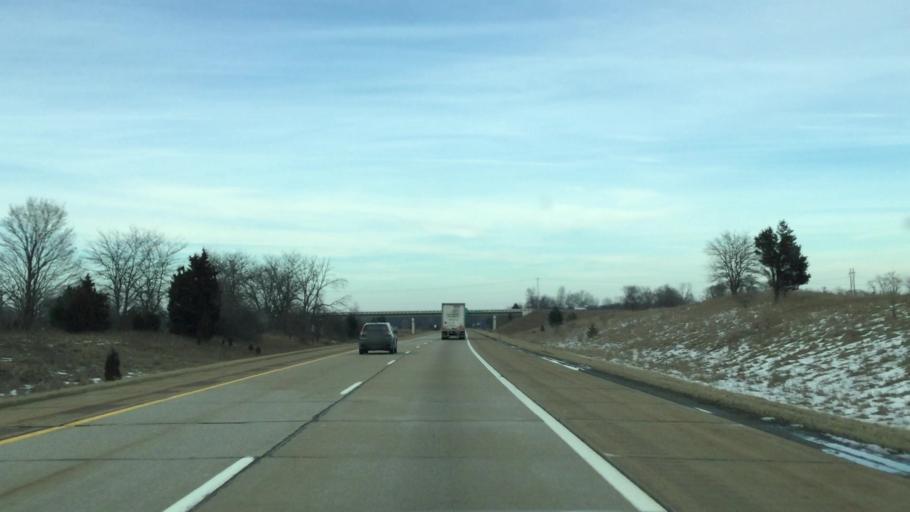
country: US
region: Michigan
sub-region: Calhoun County
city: Marshall
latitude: 42.3301
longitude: -84.9888
